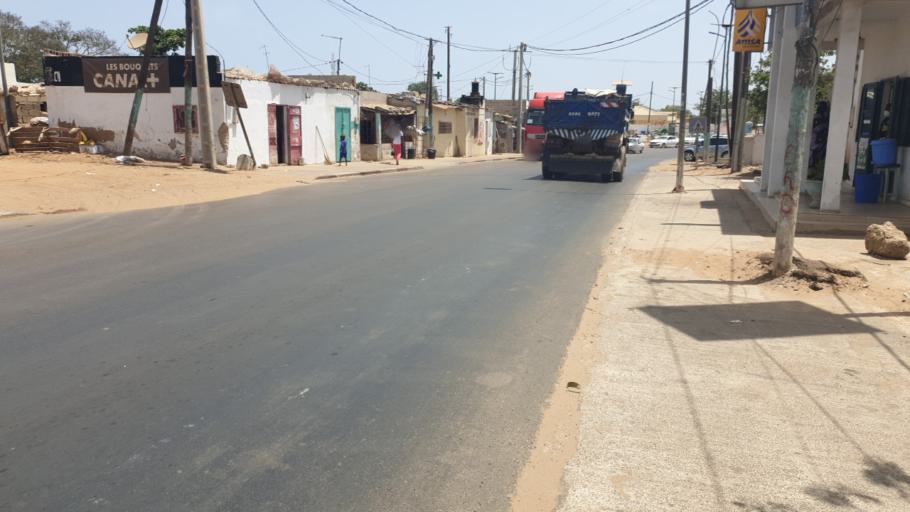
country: SN
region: Thies
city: Thies
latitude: 14.7769
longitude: -17.2256
